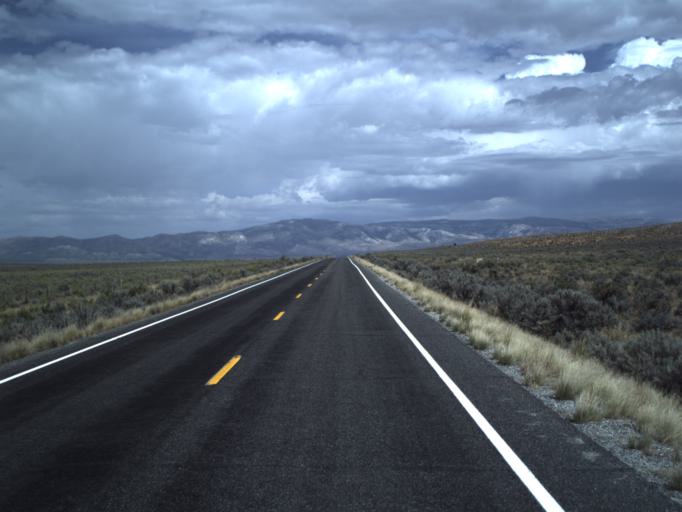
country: US
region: Idaho
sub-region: Cassia County
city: Burley
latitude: 41.6772
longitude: -113.5419
